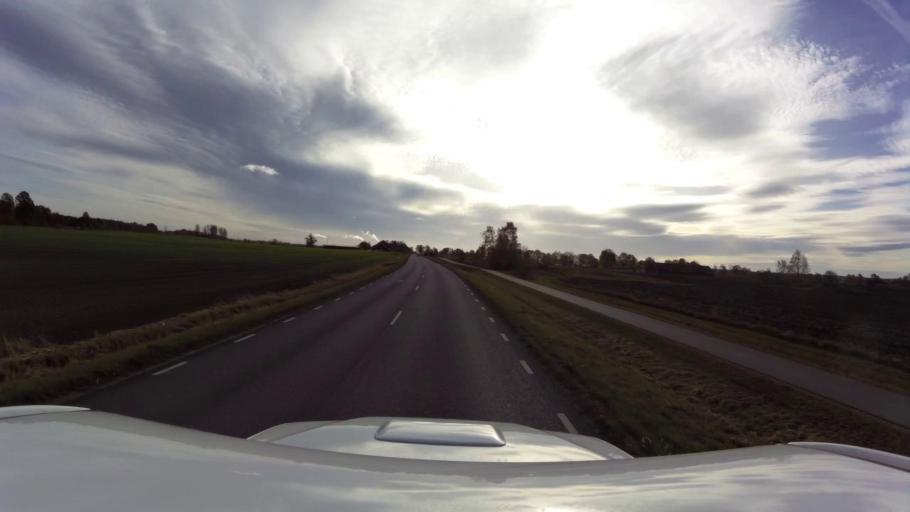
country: SE
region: OEstergoetland
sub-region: Linkopings Kommun
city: Ekangen
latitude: 58.4574
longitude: 15.6404
